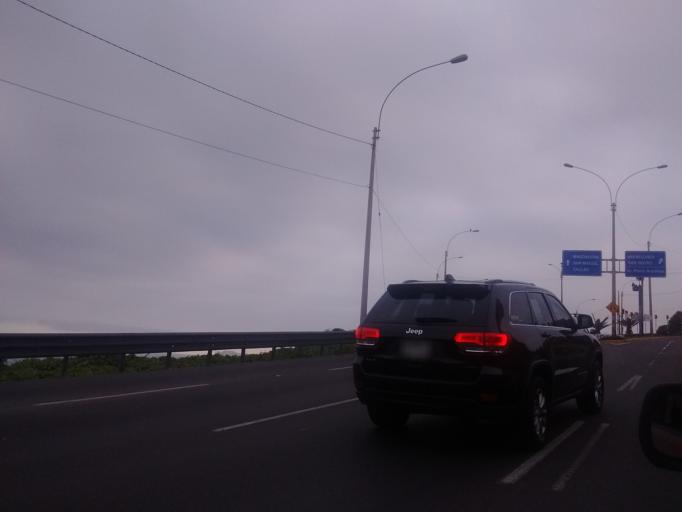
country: PE
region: Lima
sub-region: Lima
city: San Isidro
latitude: -12.1107
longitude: -77.0538
